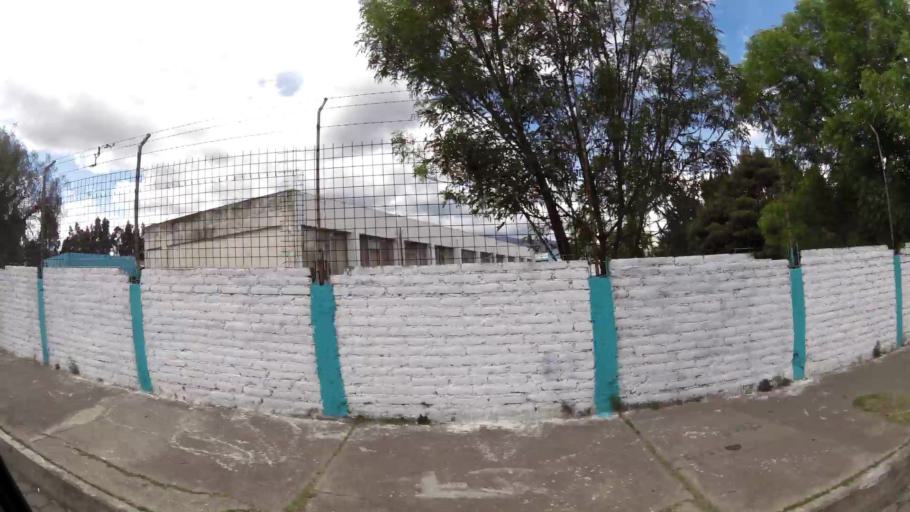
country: EC
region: Tungurahua
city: Ambato
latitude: -1.2599
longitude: -78.6154
